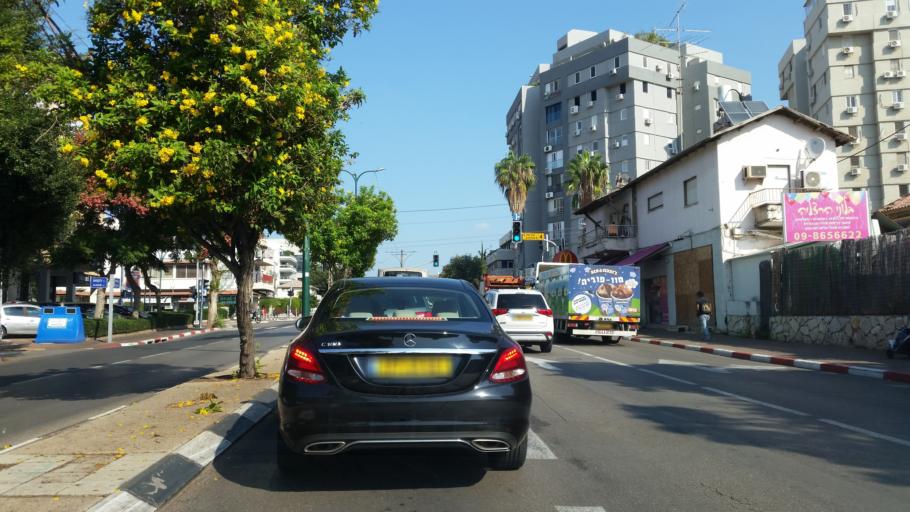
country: IL
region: Tel Aviv
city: Ramat HaSharon
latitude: 32.1603
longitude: 34.8425
